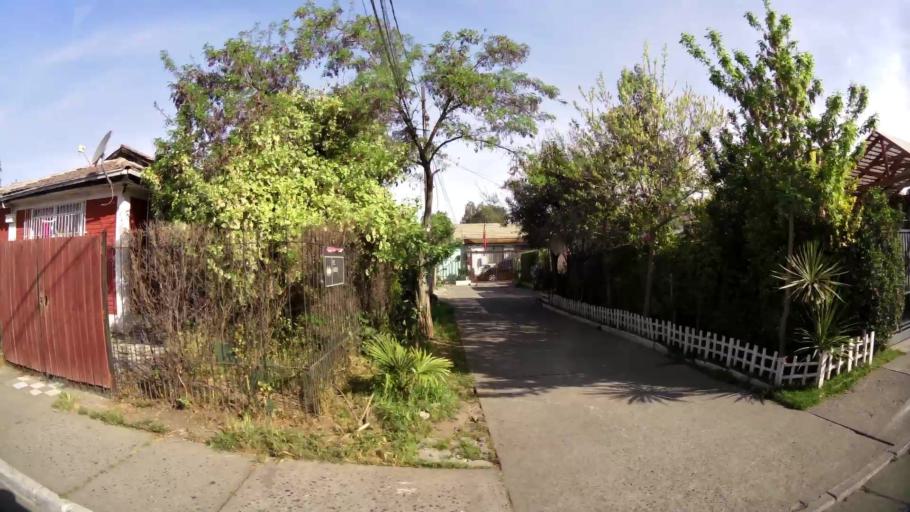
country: CL
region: Santiago Metropolitan
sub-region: Provincia de Santiago
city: Santiago
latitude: -33.5146
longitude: -70.6337
